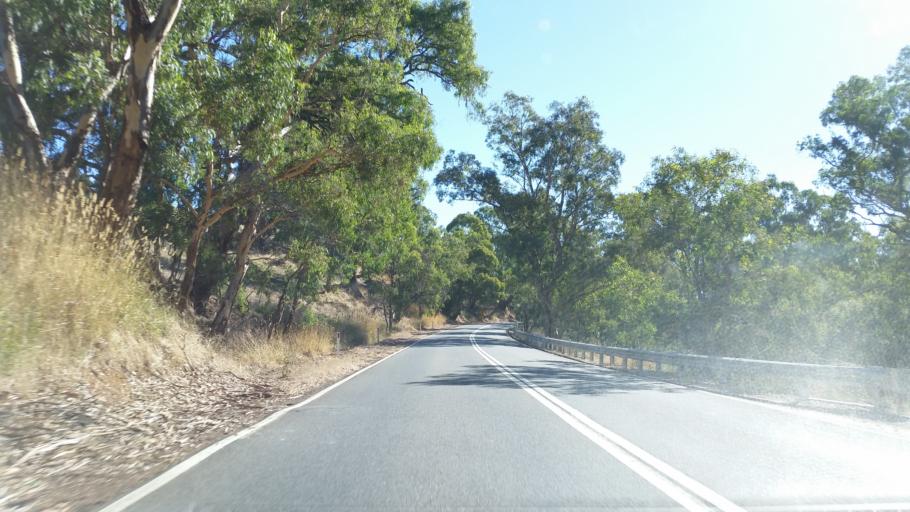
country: AU
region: South Australia
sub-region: Adelaide Hills
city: Birdwood
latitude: -34.8254
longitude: 138.9338
